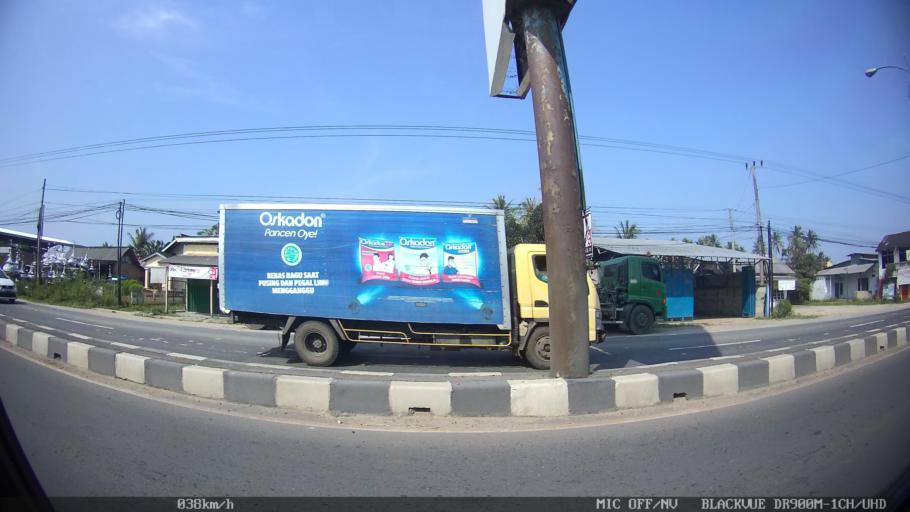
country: ID
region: Lampung
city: Natar
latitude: -5.2477
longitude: 105.1785
